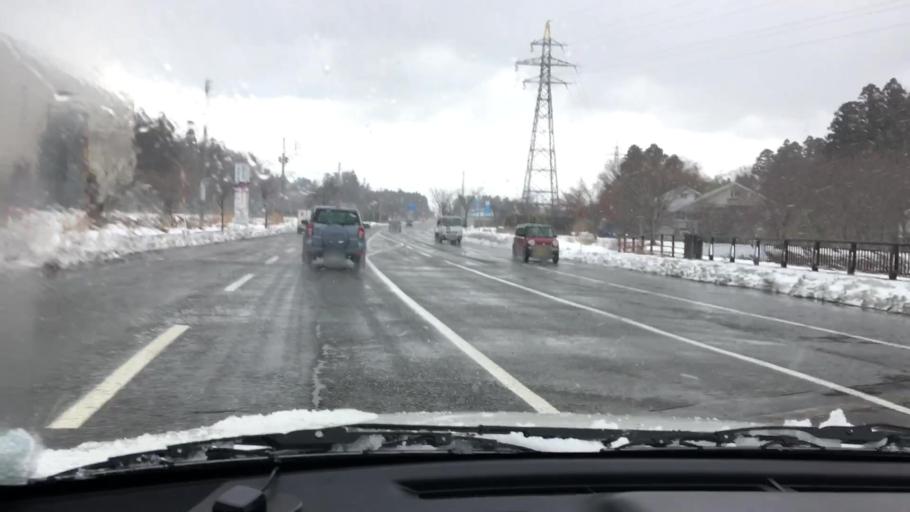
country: JP
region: Niigata
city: Joetsu
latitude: 37.0984
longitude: 138.2309
